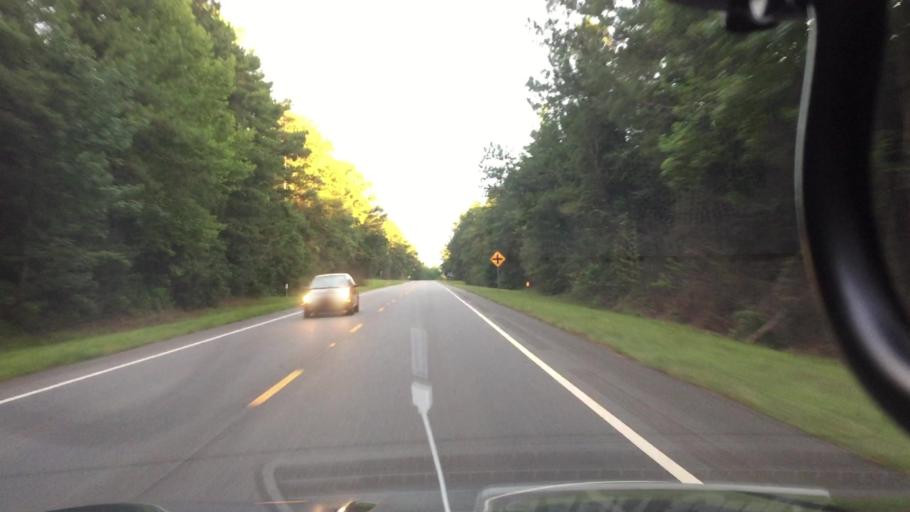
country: US
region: Alabama
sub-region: Pike County
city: Brundidge
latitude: 31.5807
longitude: -85.9341
